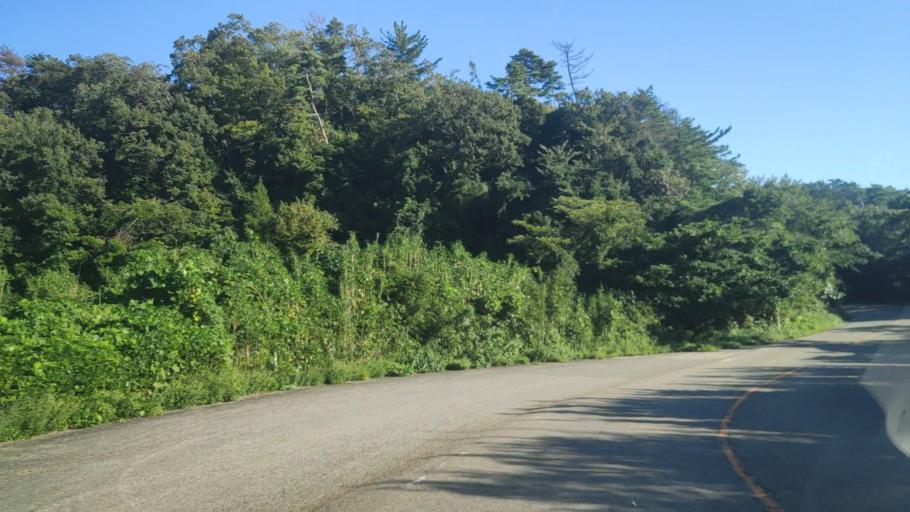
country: JP
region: Ishikawa
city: Nanao
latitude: 37.1003
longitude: 136.9499
